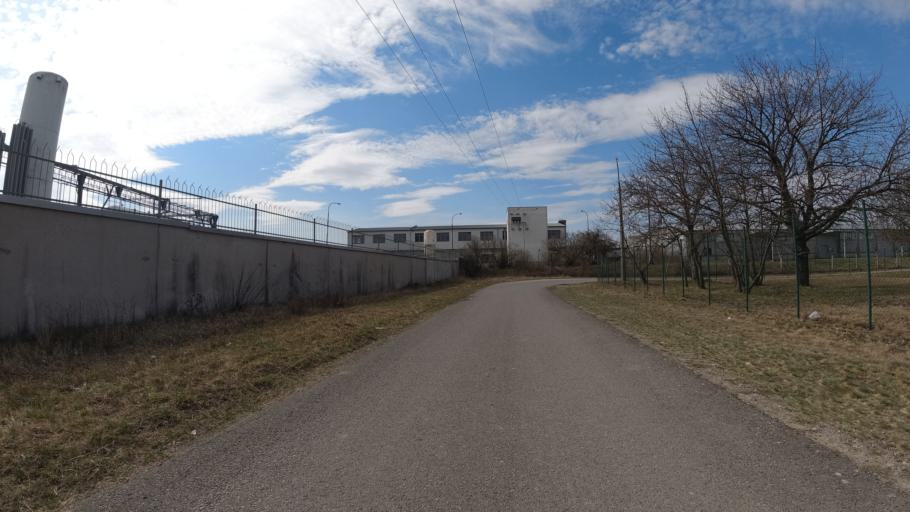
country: SK
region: Trnavsky
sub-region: Okres Trnava
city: Piestany
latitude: 48.6603
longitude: 17.8523
